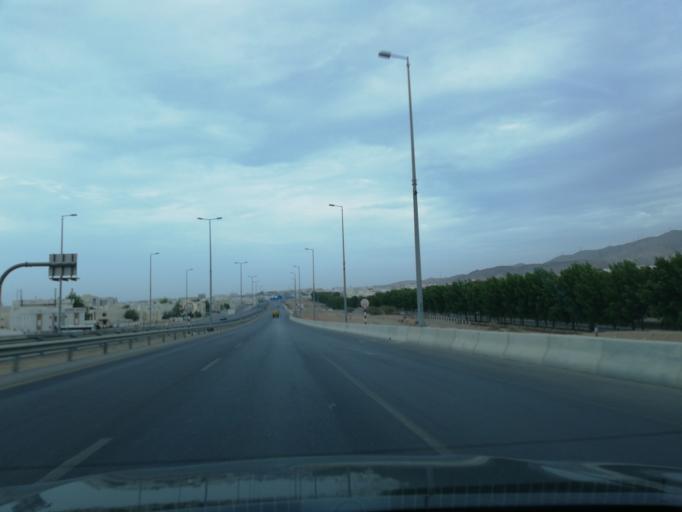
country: OM
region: Muhafazat Masqat
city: Bawshar
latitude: 23.5870
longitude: 58.4320
